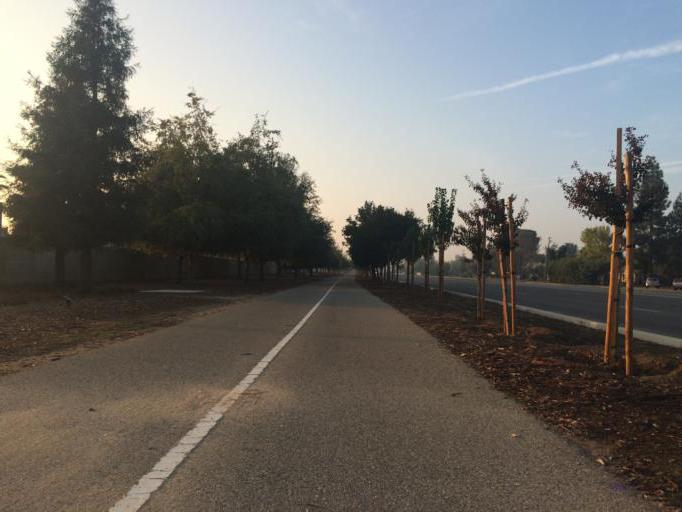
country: US
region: California
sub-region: Fresno County
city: Tarpey Village
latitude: 36.8000
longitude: -119.7004
